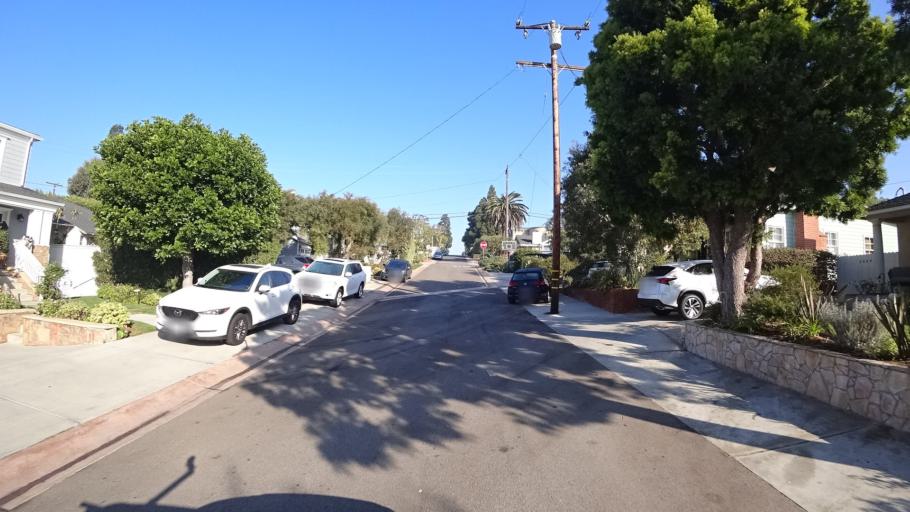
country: US
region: California
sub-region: Los Angeles County
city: Manhattan Beach
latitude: 33.8953
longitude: -118.3978
